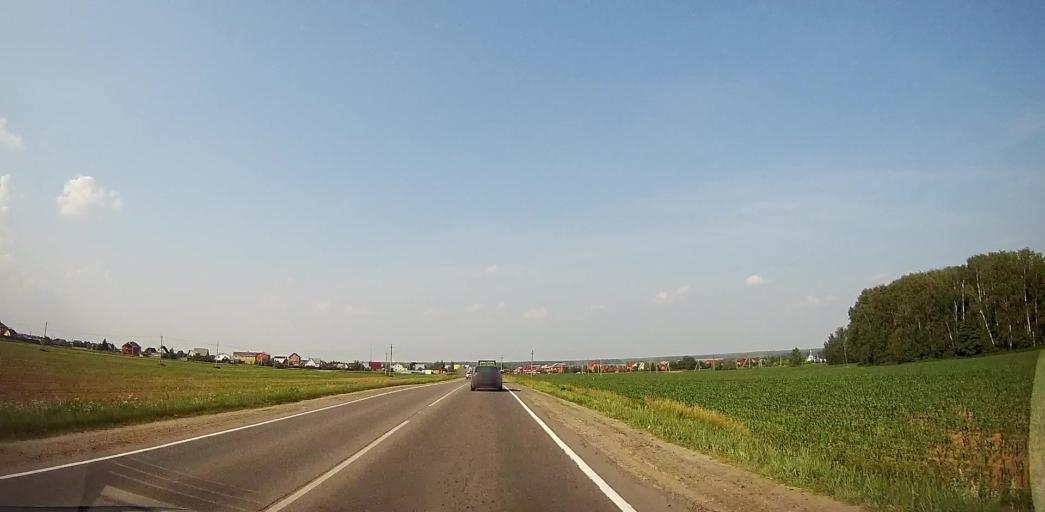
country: RU
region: Moskovskaya
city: Zhitnevo
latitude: 55.3336
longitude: 37.9064
